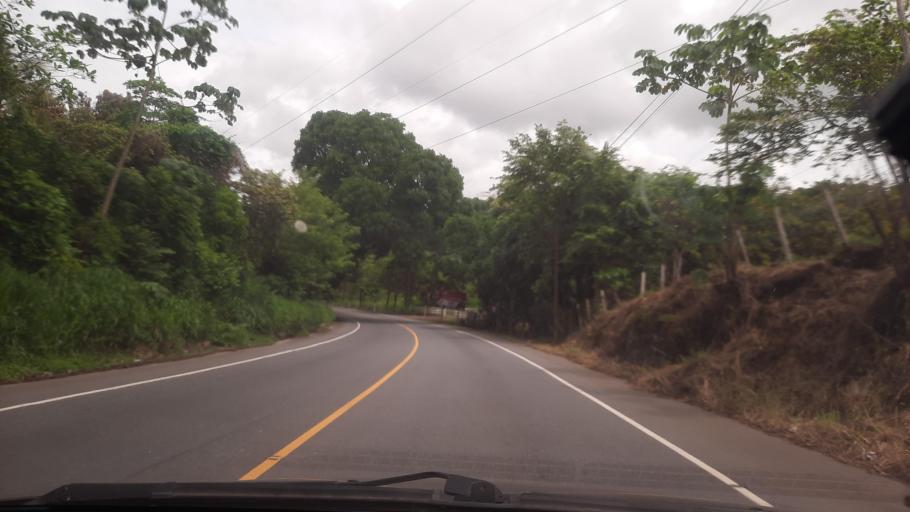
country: GT
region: Izabal
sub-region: Municipio de Los Amates
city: Los Amates
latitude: 15.2340
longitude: -89.2000
